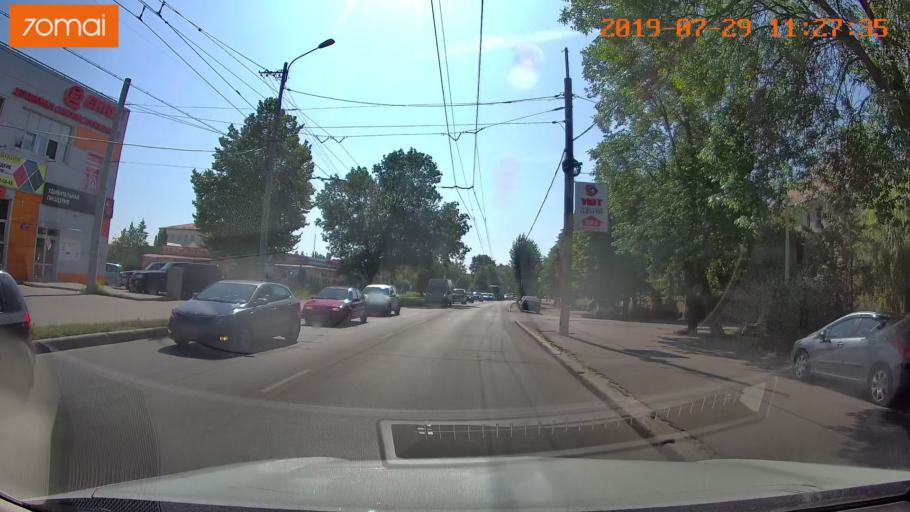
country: RU
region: Kaliningrad
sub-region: Gorod Kaliningrad
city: Kaliningrad
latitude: 54.6906
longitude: 20.5304
